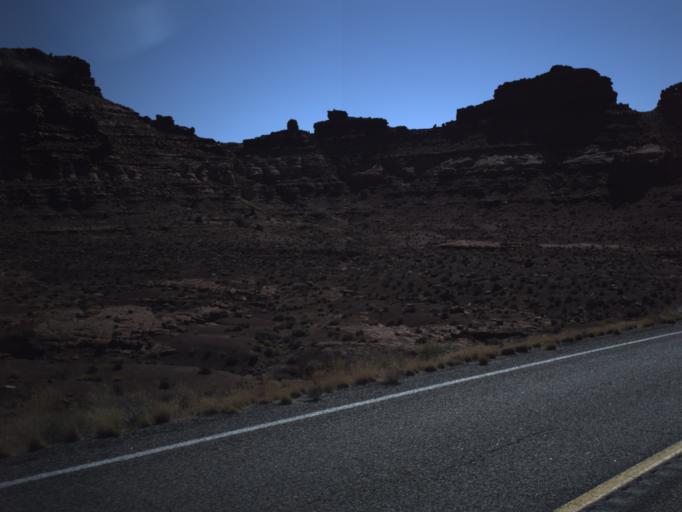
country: US
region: Utah
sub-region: San Juan County
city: Blanding
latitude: 37.8551
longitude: -110.3532
